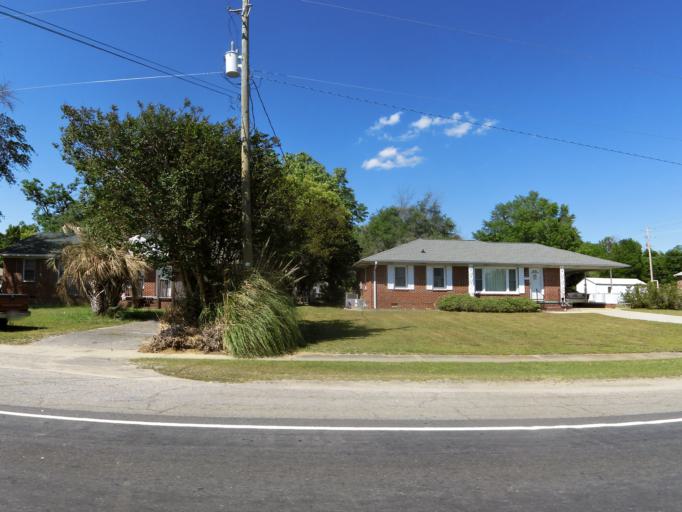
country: US
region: South Carolina
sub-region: Barnwell County
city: Williston
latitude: 33.4046
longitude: -81.4390
